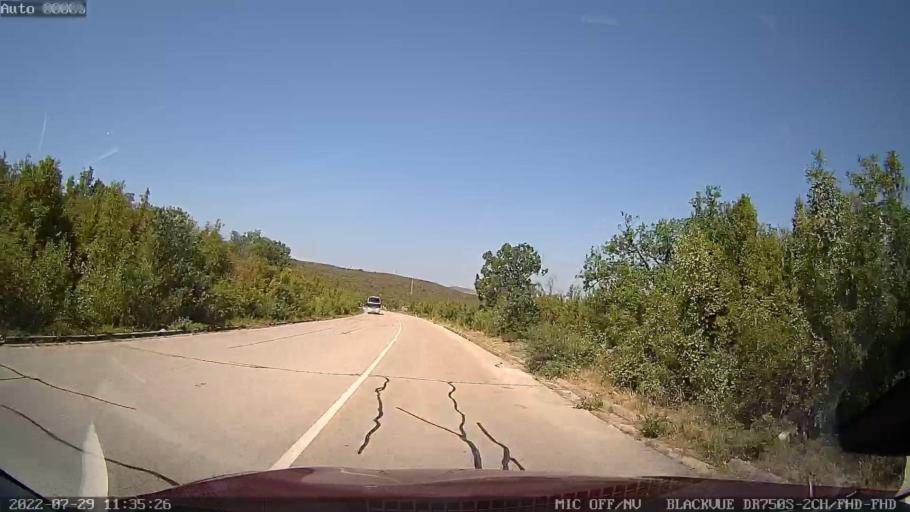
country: HR
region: Zadarska
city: Obrovac
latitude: 44.1827
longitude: 15.7124
